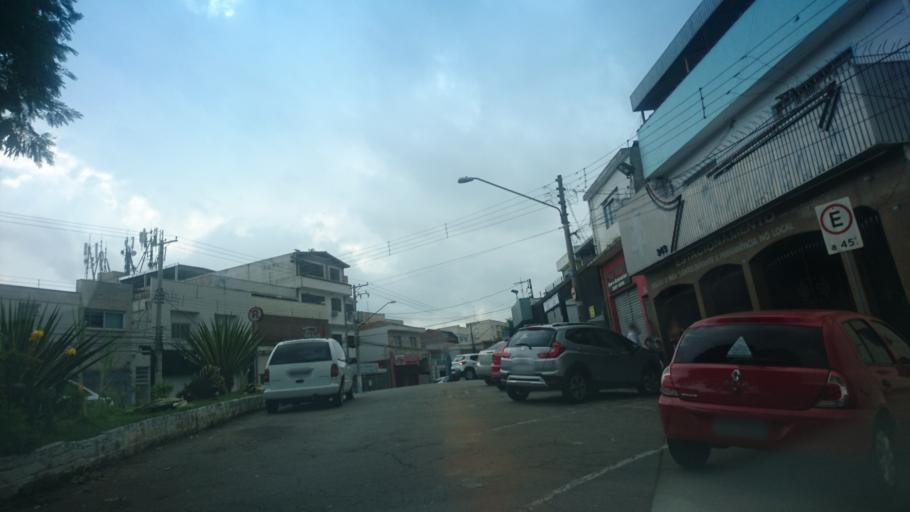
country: BR
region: Sao Paulo
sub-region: Guarulhos
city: Guarulhos
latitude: -23.4571
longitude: -46.5260
